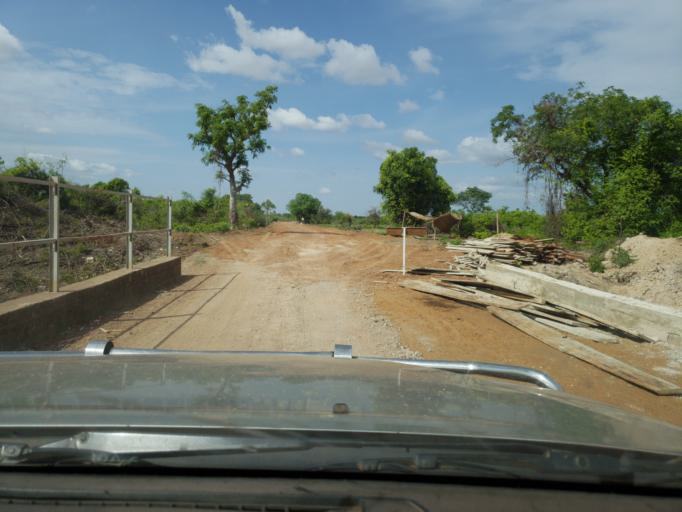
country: ML
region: Segou
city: Bla
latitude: 12.7711
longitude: -5.6167
